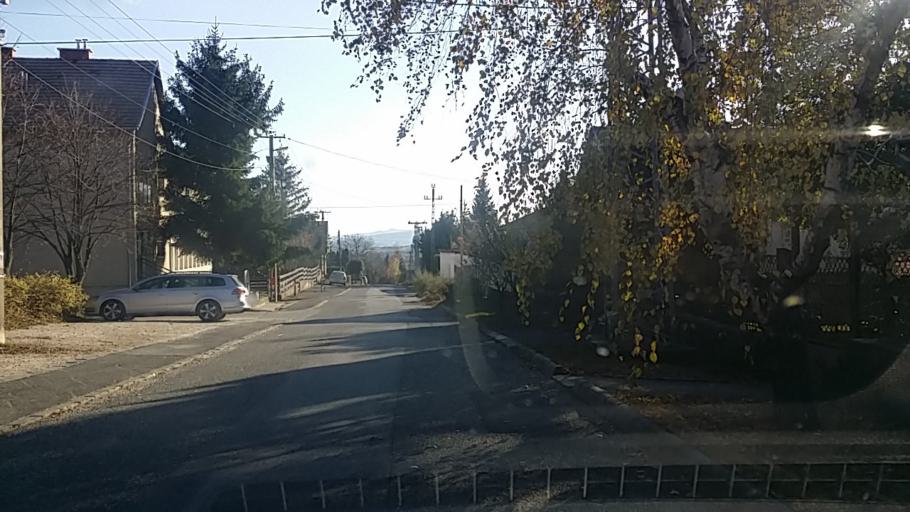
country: HU
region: Pest
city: Pilisszanto
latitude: 47.6693
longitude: 18.8846
